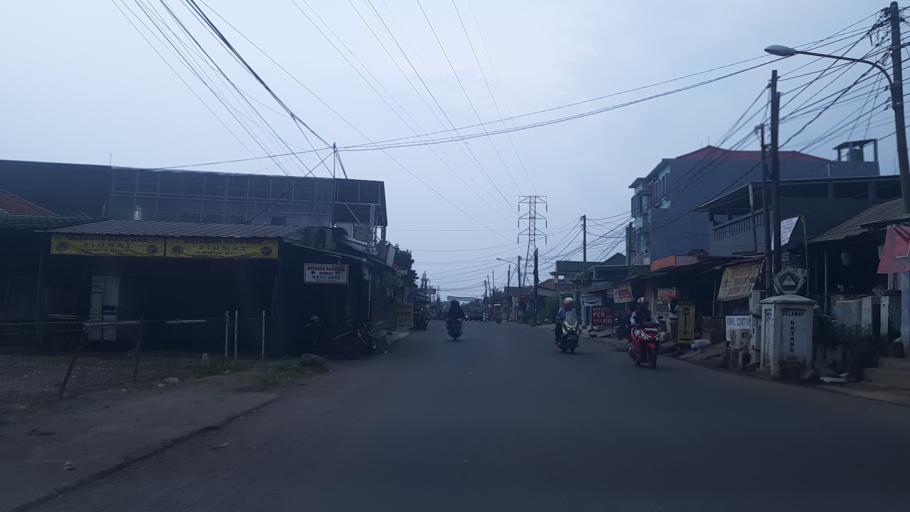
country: ID
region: West Java
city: Cibinong
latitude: -6.5242
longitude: 106.8581
